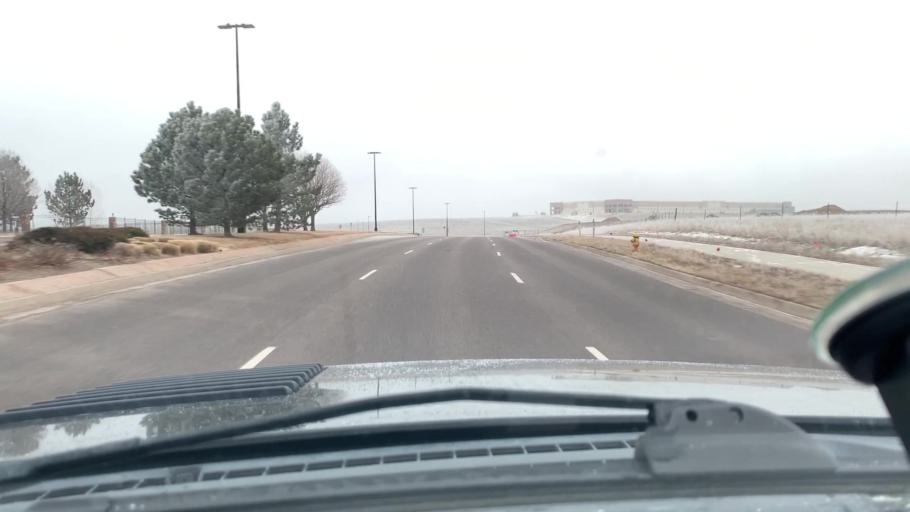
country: US
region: Colorado
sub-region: Arapahoe County
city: Dove Valley
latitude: 39.5778
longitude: -104.8218
